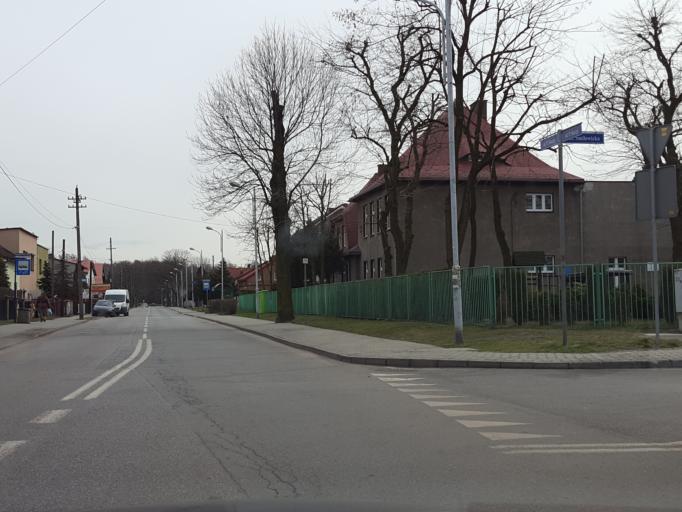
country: PL
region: Silesian Voivodeship
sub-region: Ruda Slaska
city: Ruda Slaska
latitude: 50.2398
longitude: 18.8382
